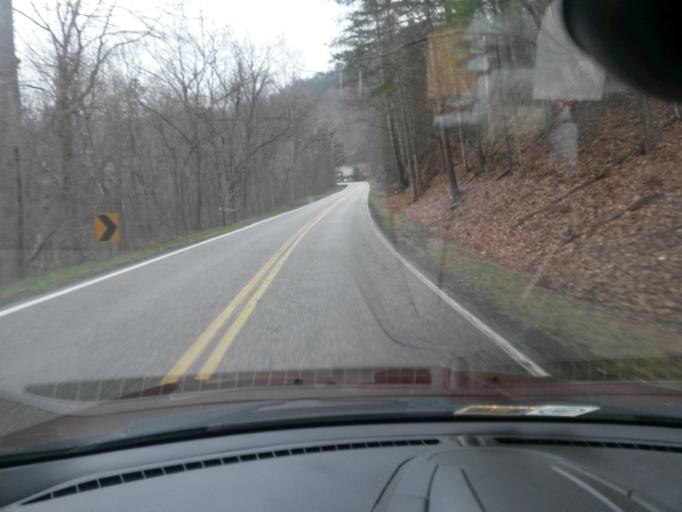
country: US
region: Virginia
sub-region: Alleghany County
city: Clifton Forge
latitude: 37.9100
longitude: -79.7328
